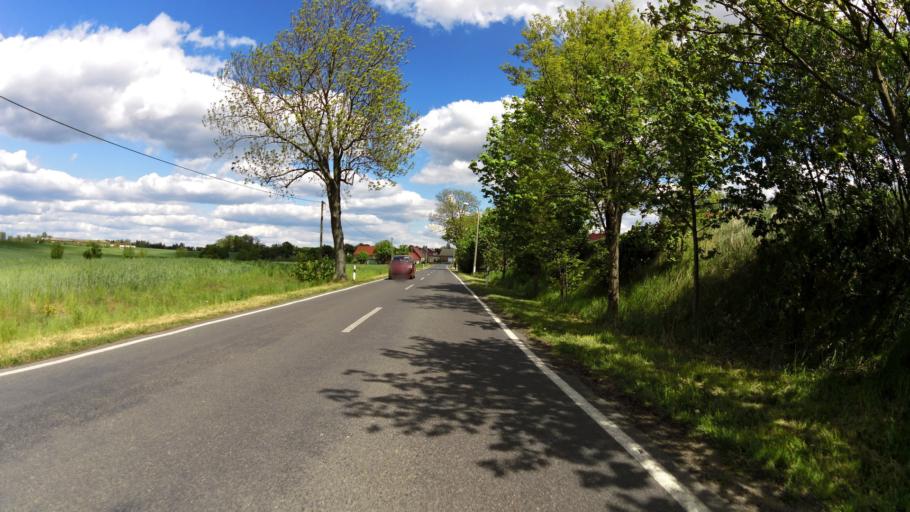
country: DE
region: Brandenburg
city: Diensdorf-Radlow
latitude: 52.1957
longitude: 14.1050
